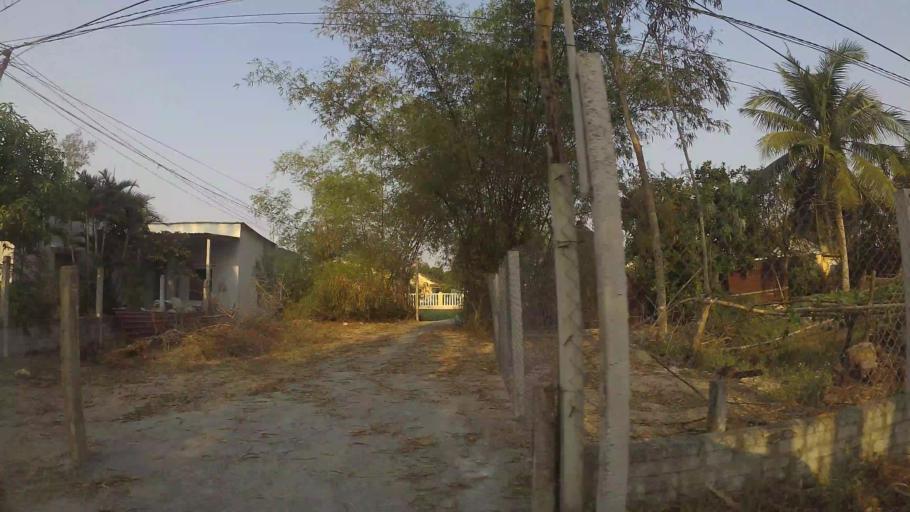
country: VN
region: Da Nang
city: Ngu Hanh Son
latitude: 15.9700
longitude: 108.2443
